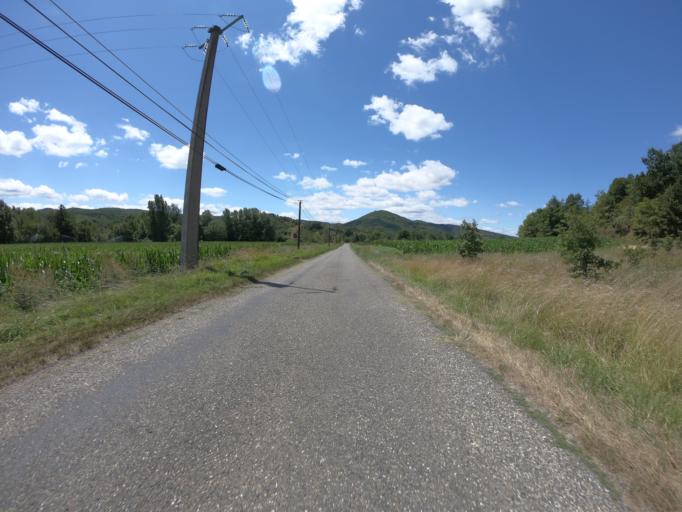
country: FR
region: Midi-Pyrenees
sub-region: Departement de l'Ariege
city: Mirepoix
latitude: 43.0471
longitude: 1.7901
